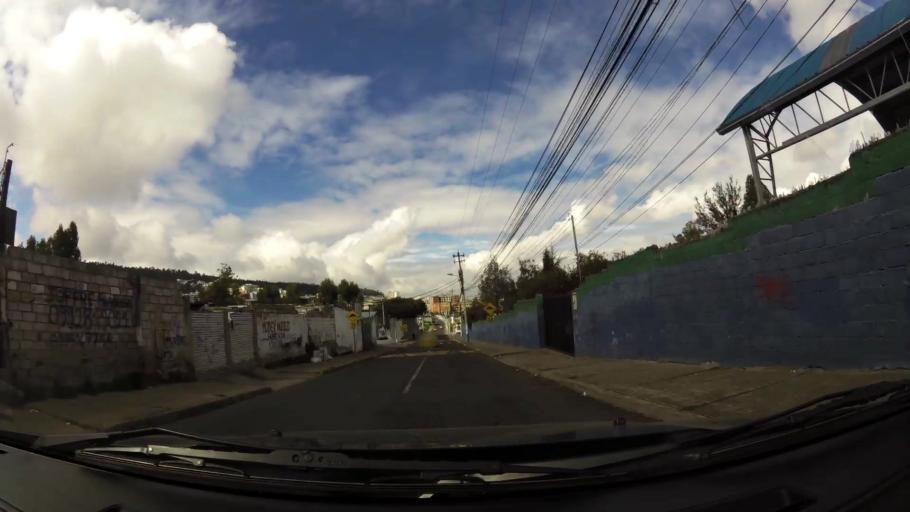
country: EC
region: Pichincha
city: Quito
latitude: -0.1611
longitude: -78.4711
